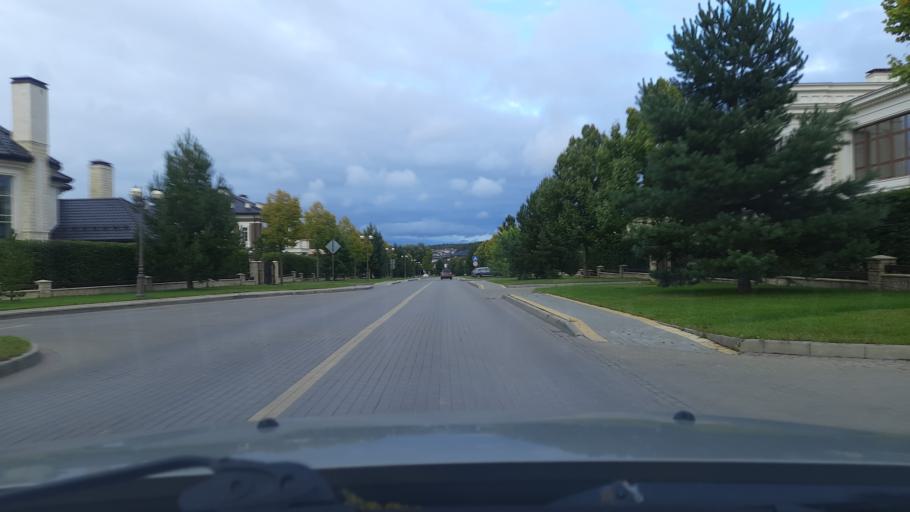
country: RU
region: Moskovskaya
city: Nikolina Gora
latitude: 55.7723
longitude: 37.0439
